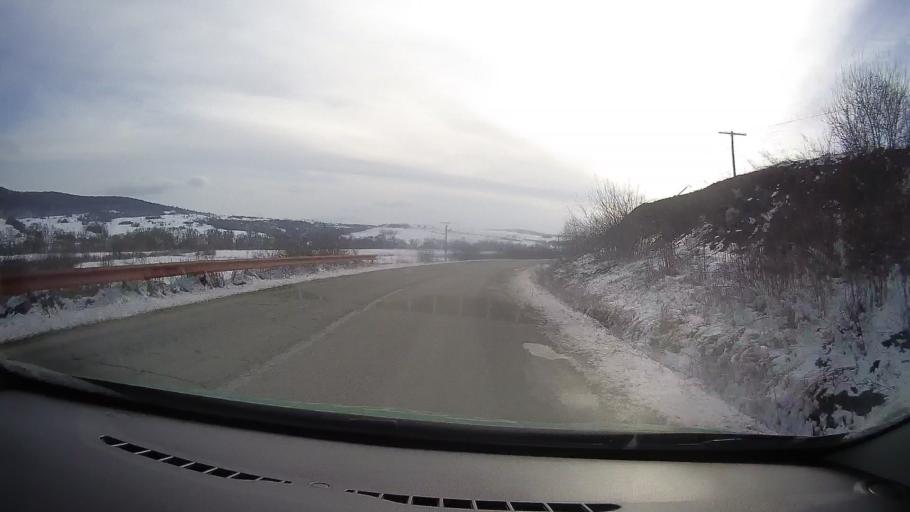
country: RO
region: Sibiu
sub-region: Comuna Iacobeni
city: Iacobeni
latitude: 46.0231
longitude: 24.7068
